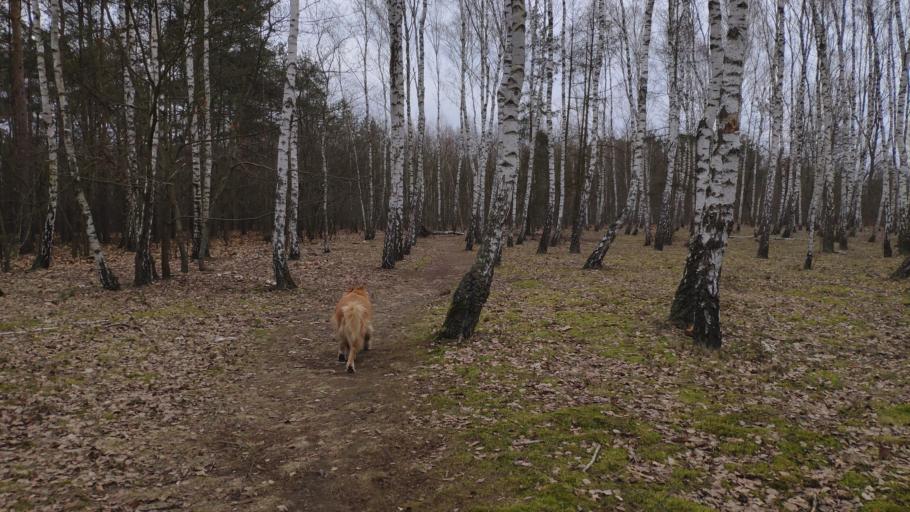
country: PL
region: Lodz Voivodeship
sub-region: Powiat pabianicki
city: Ksawerow
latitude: 51.7248
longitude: 19.3888
